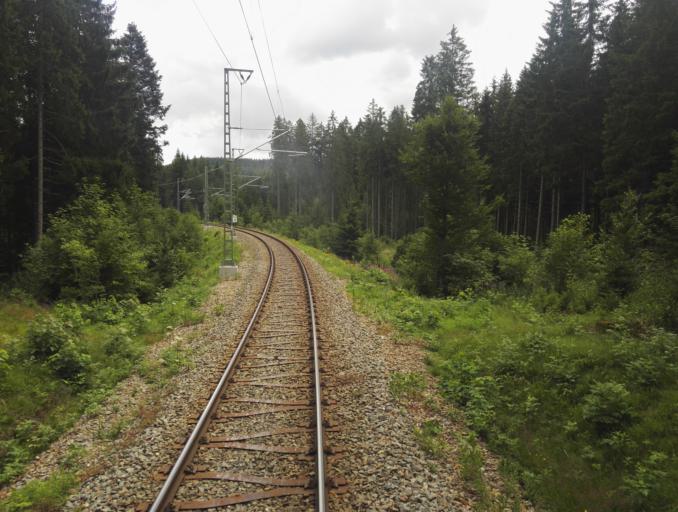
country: DE
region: Baden-Wuerttemberg
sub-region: Freiburg Region
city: Hinterzarten
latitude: 47.8551
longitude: 8.1212
